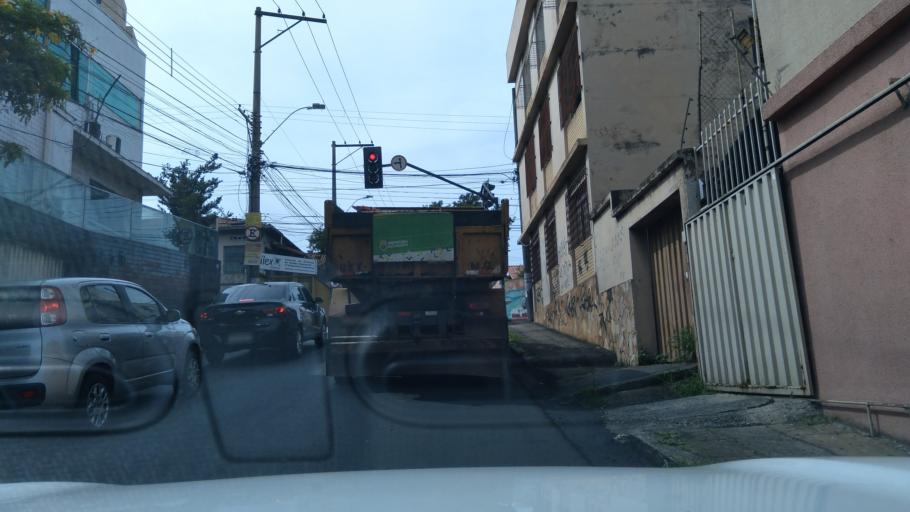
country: BR
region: Minas Gerais
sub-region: Belo Horizonte
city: Belo Horizonte
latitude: -19.9111
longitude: -43.9643
